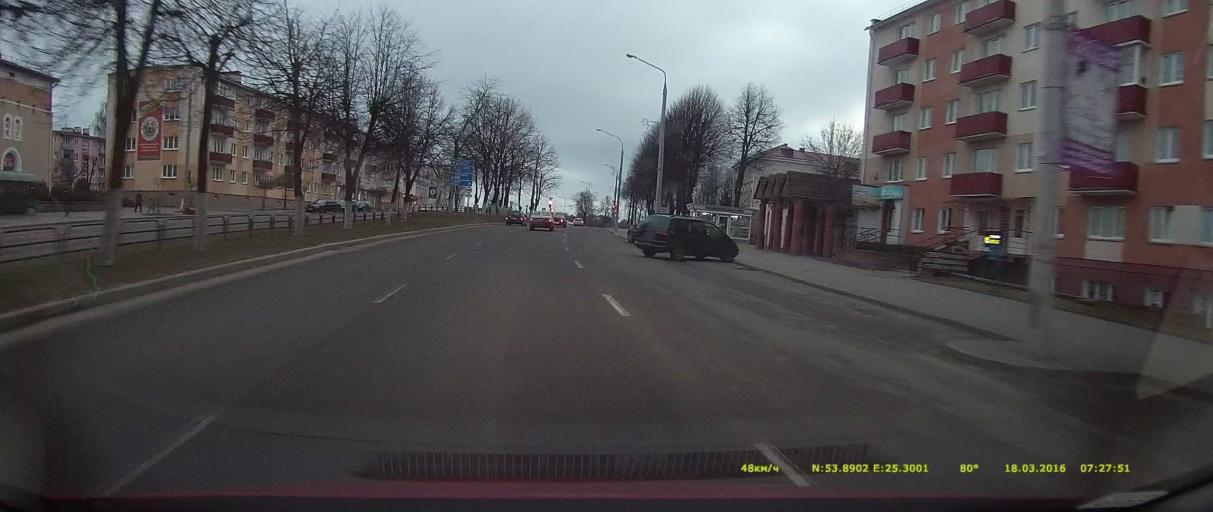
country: BY
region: Grodnenskaya
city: Lida
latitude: 53.8901
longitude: 25.3003
